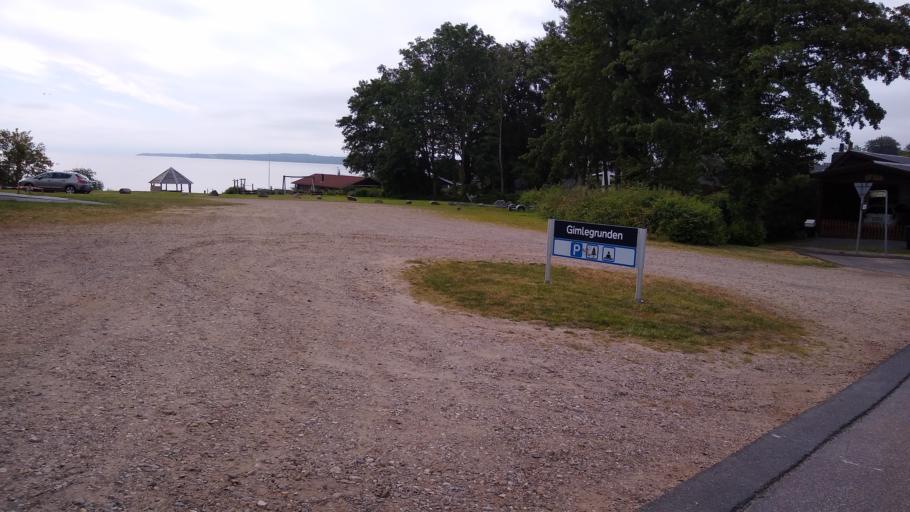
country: DK
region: South Denmark
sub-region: Vejle Kommune
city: Brejning
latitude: 55.6477
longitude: 9.7404
